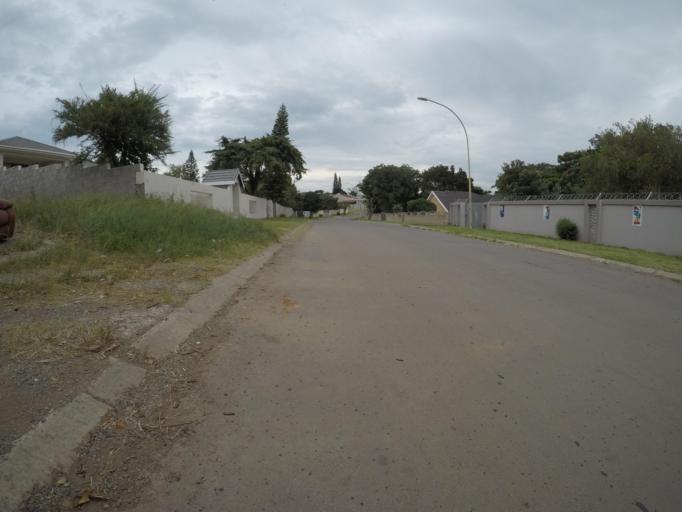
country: ZA
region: Eastern Cape
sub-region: Buffalo City Metropolitan Municipality
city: East London
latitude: -33.0029
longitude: 27.8591
